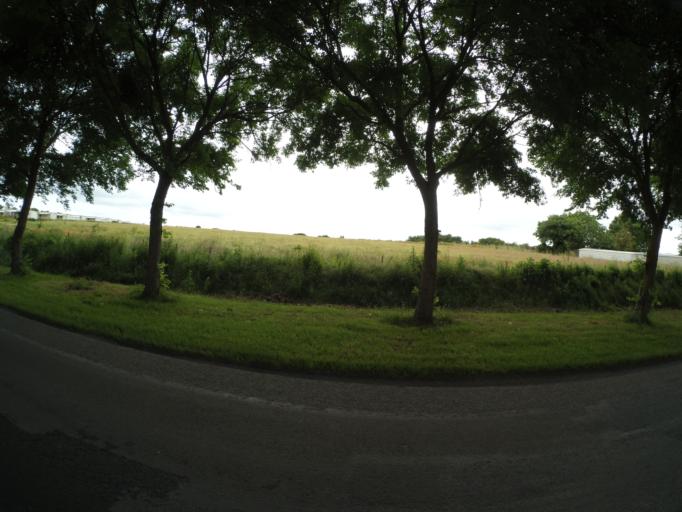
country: FR
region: Poitou-Charentes
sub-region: Departement de la Charente-Maritime
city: Saint-Laurent-de-la-Pree
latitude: 45.9883
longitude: -1.0153
